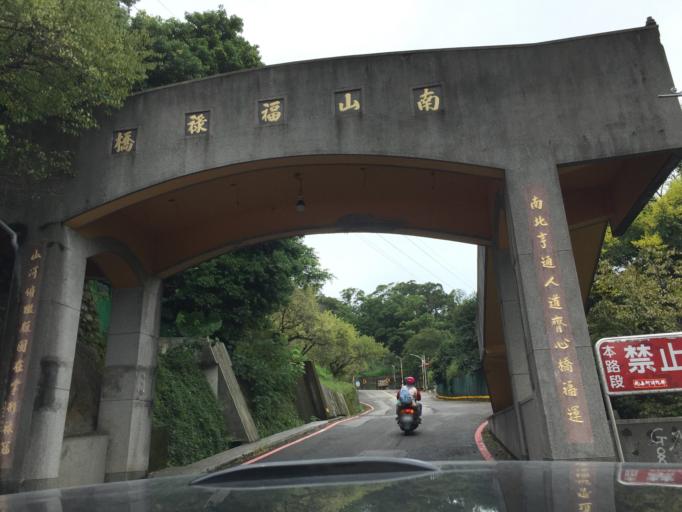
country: TW
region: Taipei
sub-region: Taipei
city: Banqiao
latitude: 24.9731
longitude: 121.4995
